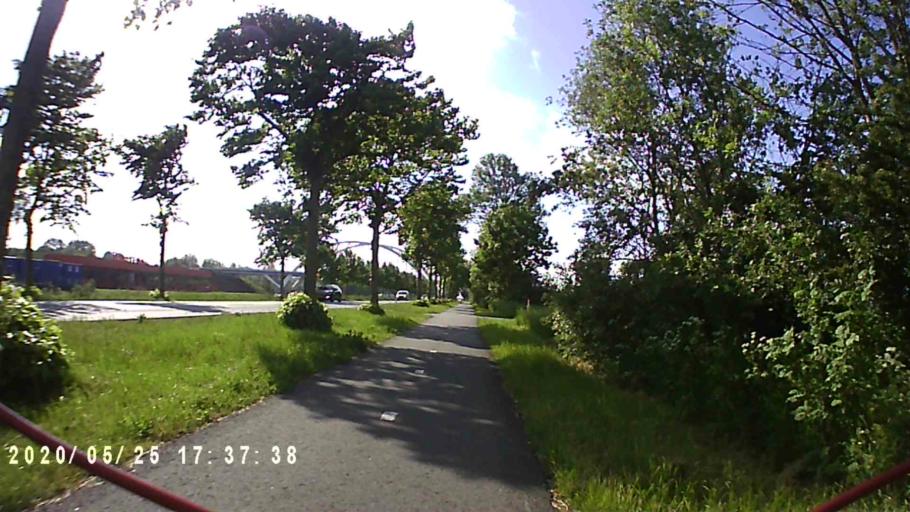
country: NL
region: Groningen
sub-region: Gemeente Groningen
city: Korrewegwijk
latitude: 53.2418
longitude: 6.5609
